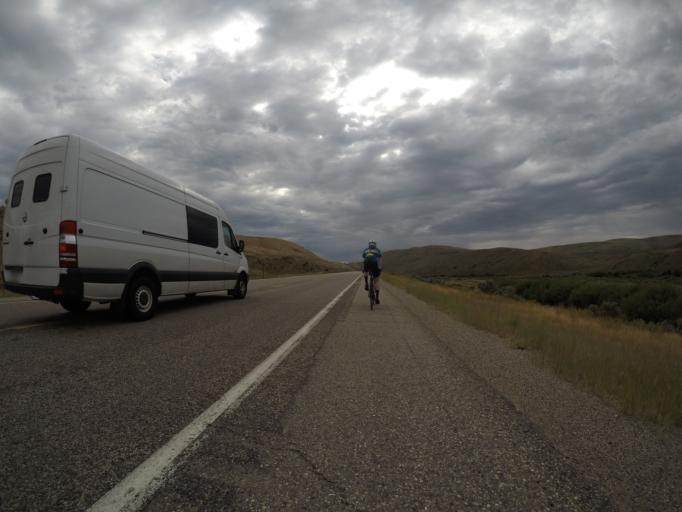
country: US
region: Wyoming
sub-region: Lincoln County
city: Kemmerer
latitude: 41.8230
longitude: -110.8717
